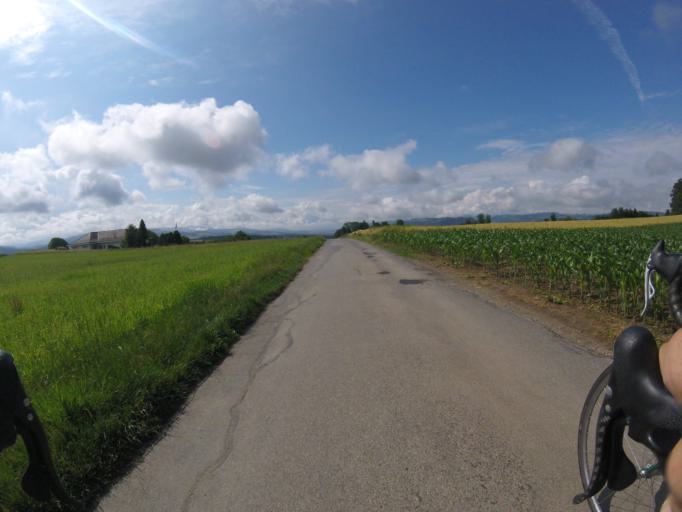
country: CH
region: Bern
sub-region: Bern-Mittelland District
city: Vechigen
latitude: 46.9387
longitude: 7.5384
